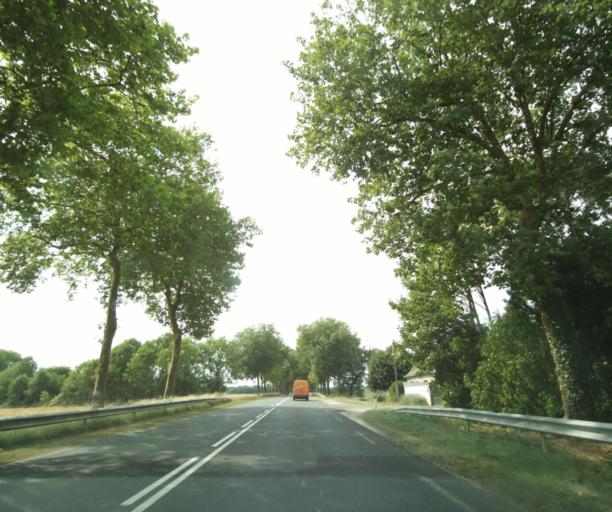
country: FR
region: Centre
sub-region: Departement d'Indre-et-Loire
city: Neuille-Pont-Pierre
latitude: 47.5238
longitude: 0.5773
